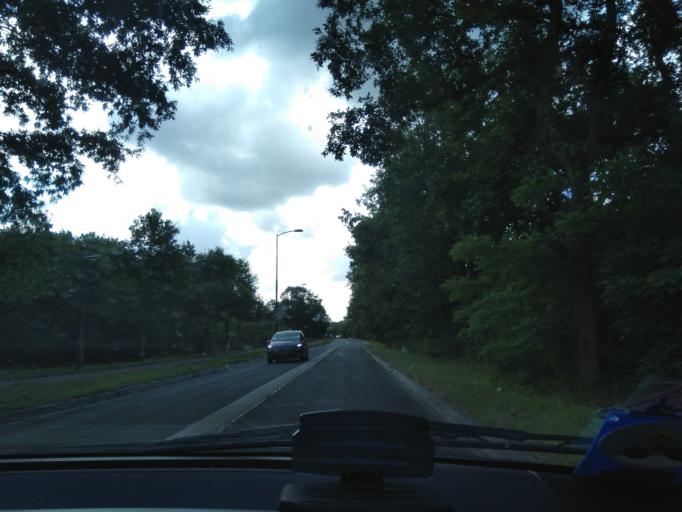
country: NL
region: North Brabant
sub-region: Gemeente Oosterhout
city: Oosterhout
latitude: 51.6192
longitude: 4.8543
